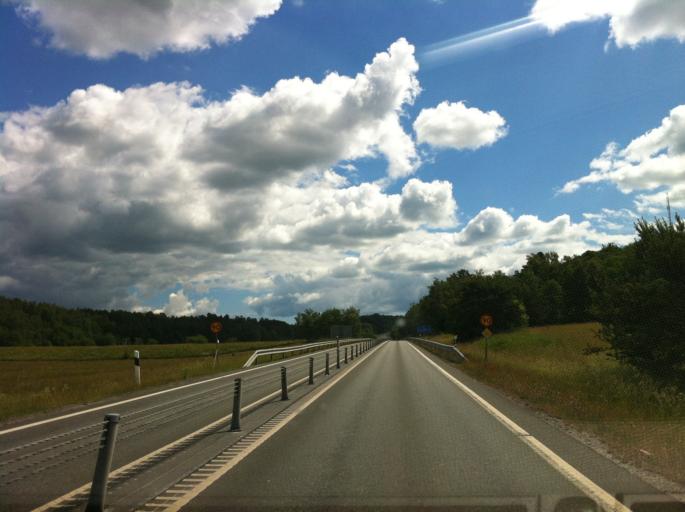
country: SE
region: Skane
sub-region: Sjobo Kommun
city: Sjoebo
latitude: 55.6244
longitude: 13.6874
